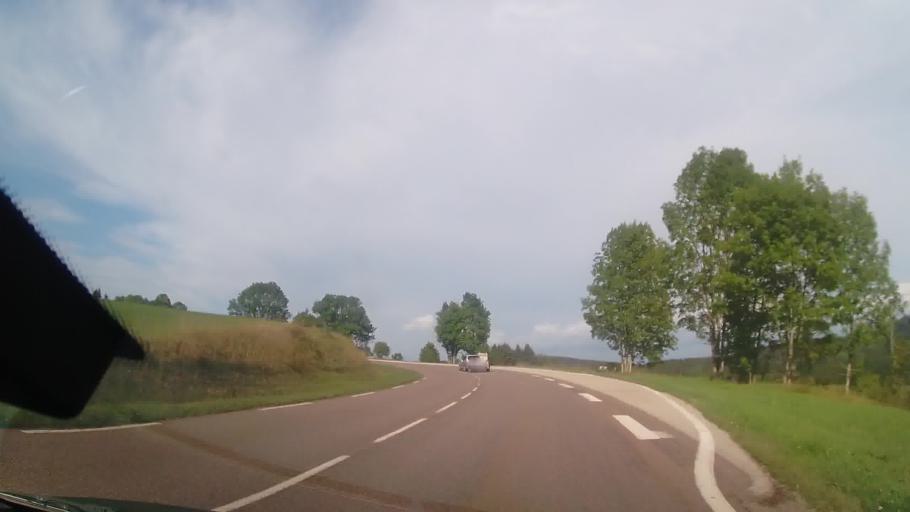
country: FR
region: Franche-Comte
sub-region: Departement du Jura
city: Morbier
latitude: 46.5991
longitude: 5.9021
